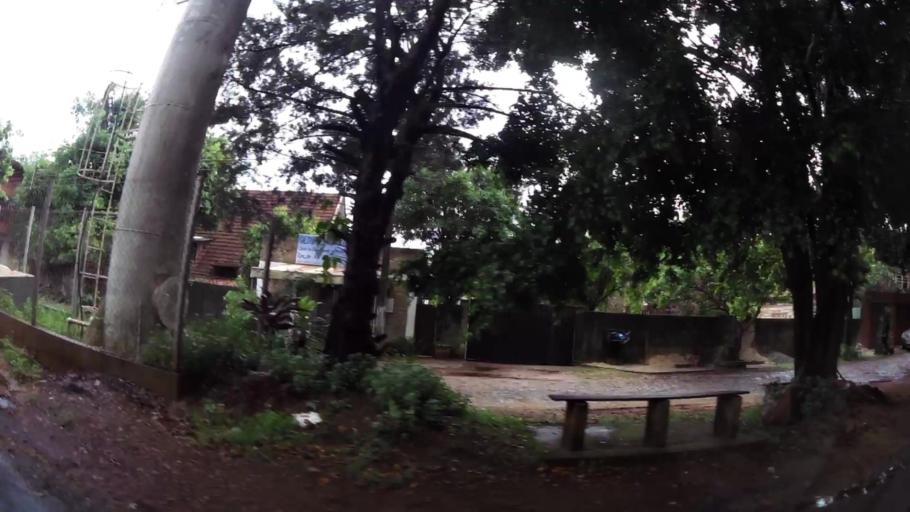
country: PY
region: Alto Parana
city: Ciudad del Este
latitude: -25.5078
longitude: -54.6447
